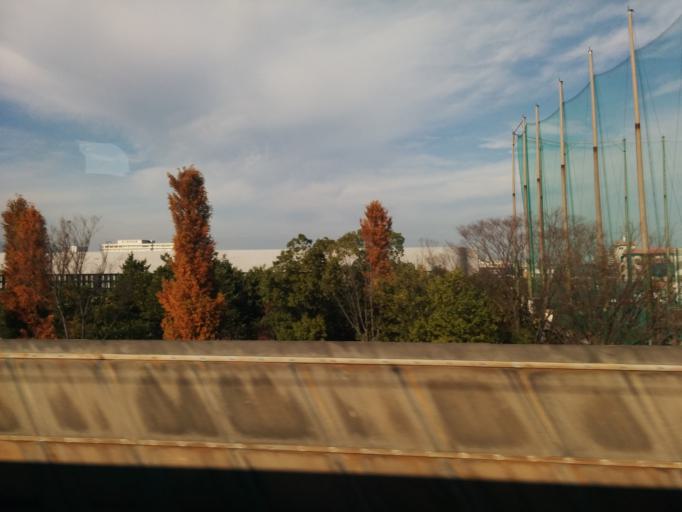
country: JP
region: Gifu
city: Ogaki
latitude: 35.3462
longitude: 136.6255
